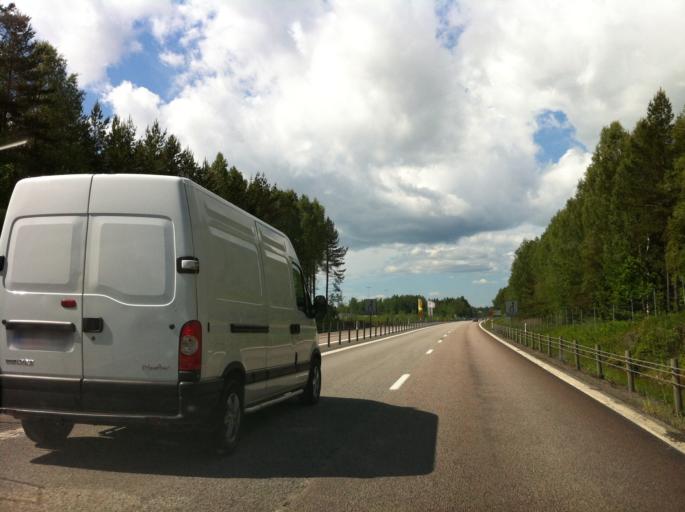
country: SE
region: Vaermland
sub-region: Saffle Kommun
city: Saeffle
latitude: 59.1306
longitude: 12.8937
